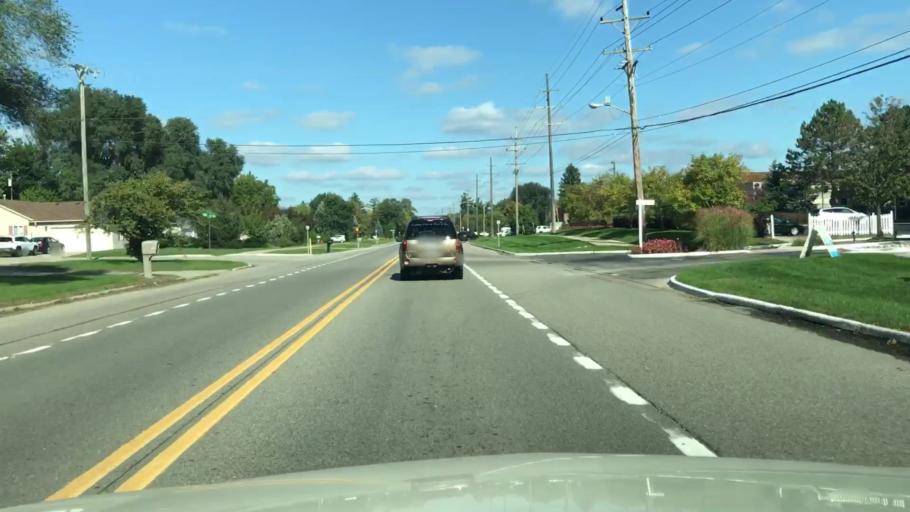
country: US
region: Michigan
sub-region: Macomb County
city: Utica
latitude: 42.6329
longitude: -83.0918
